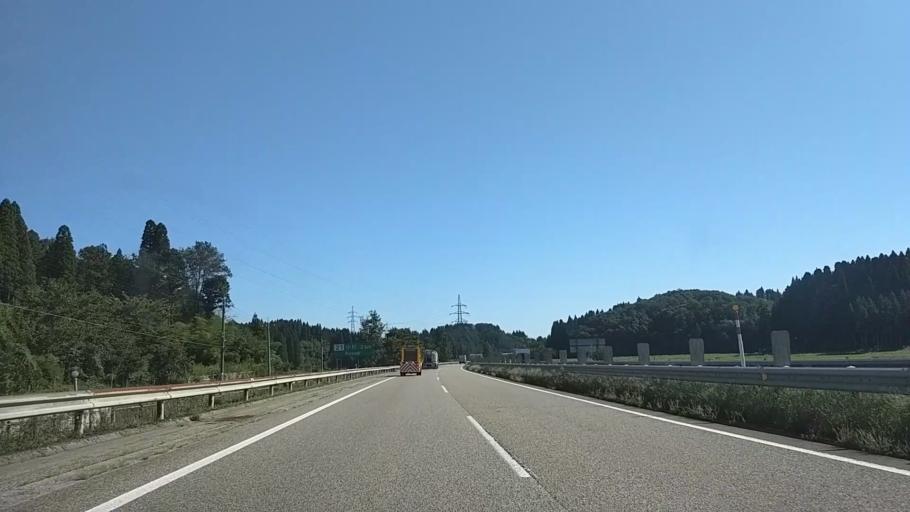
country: JP
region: Toyama
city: Takaoka
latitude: 36.6866
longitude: 137.0576
